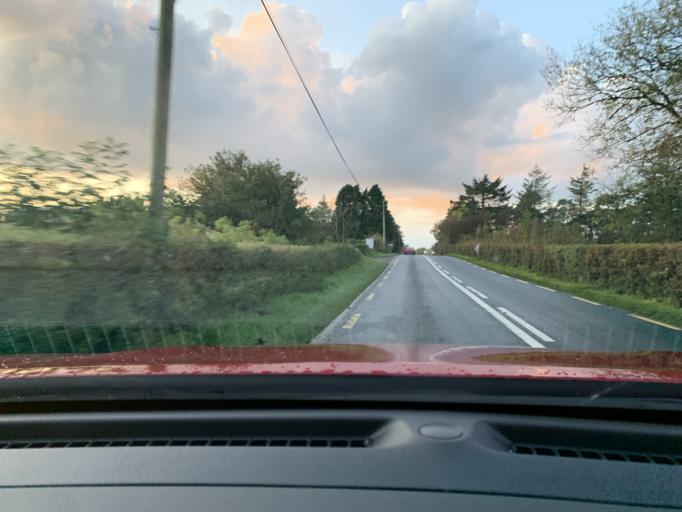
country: IE
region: Connaught
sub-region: Sligo
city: Ballymote
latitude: 54.1059
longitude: -8.4119
